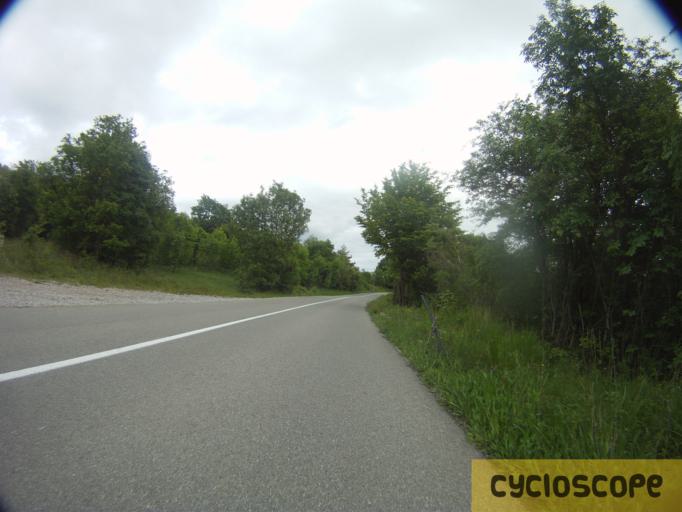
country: HR
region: Primorsko-Goranska
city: Klana
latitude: 45.4736
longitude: 14.2927
